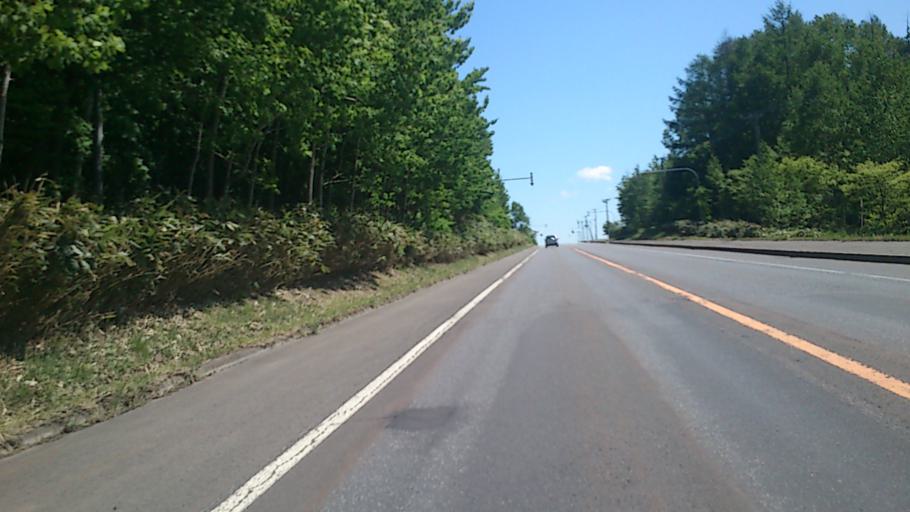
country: JP
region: Hokkaido
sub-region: Asahikawa-shi
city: Asahikawa
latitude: 44.0559
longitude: 142.4048
